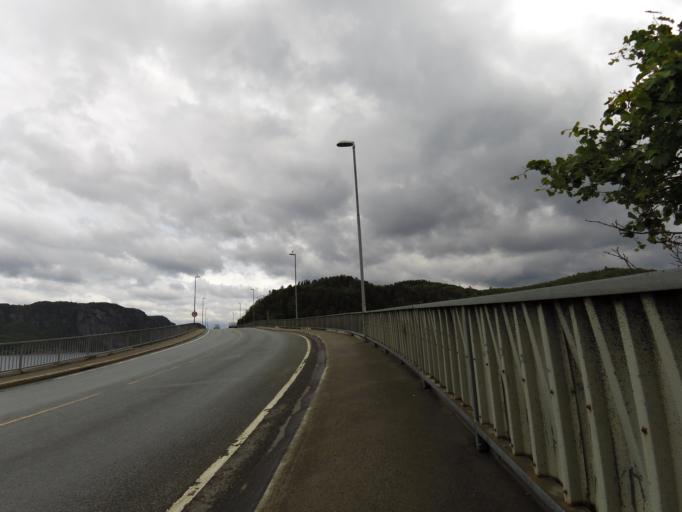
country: NO
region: Vest-Agder
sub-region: Farsund
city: Farsund
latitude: 58.0947
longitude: 6.8117
